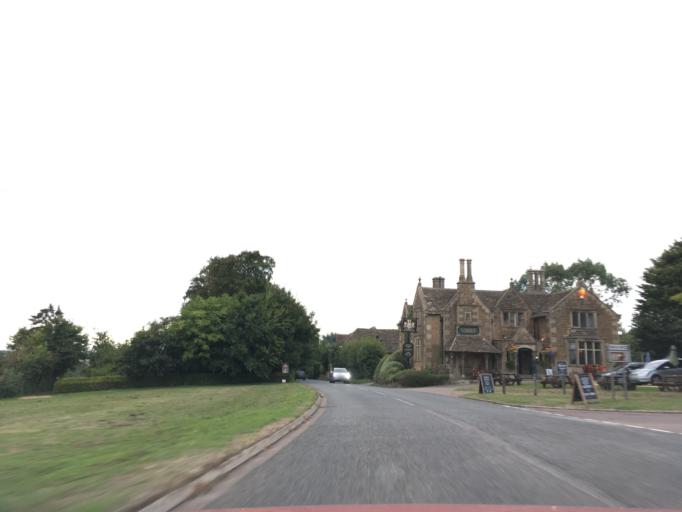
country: GB
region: England
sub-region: Wiltshire
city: Bremhill
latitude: 51.4335
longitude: -2.0638
